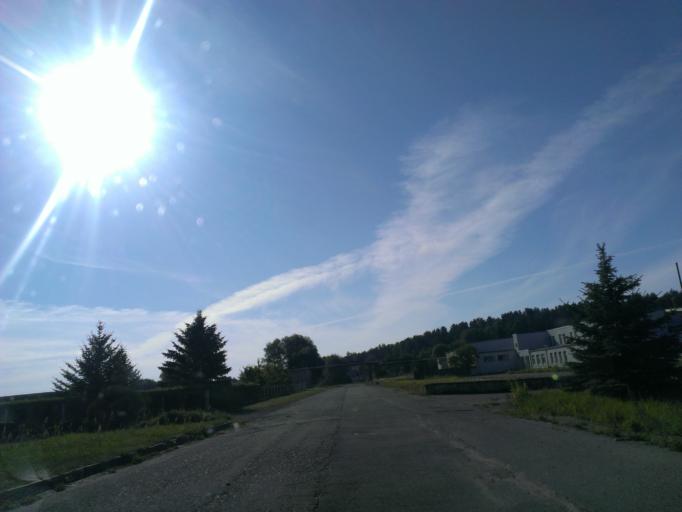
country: LV
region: Adazi
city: Adazi
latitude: 57.0630
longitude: 24.3293
